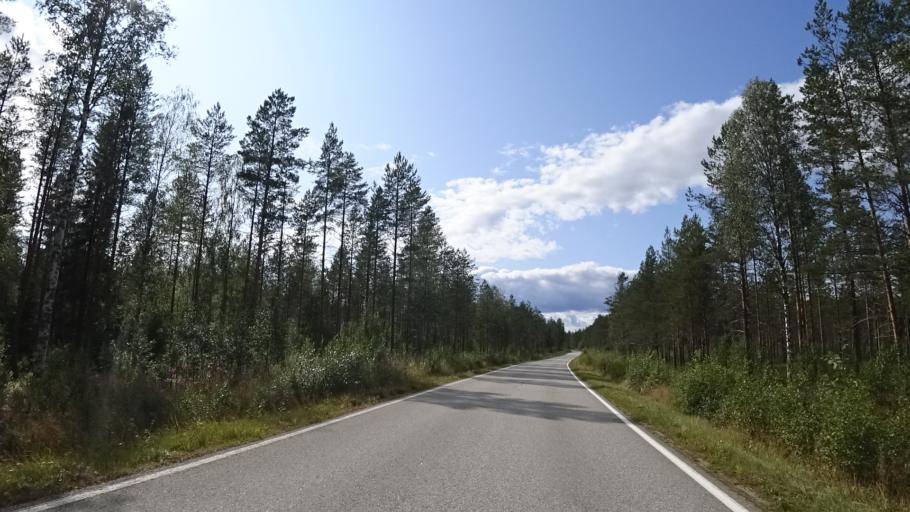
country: FI
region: North Karelia
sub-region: Joensuu
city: Ilomantsi
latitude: 62.4125
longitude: 30.9938
